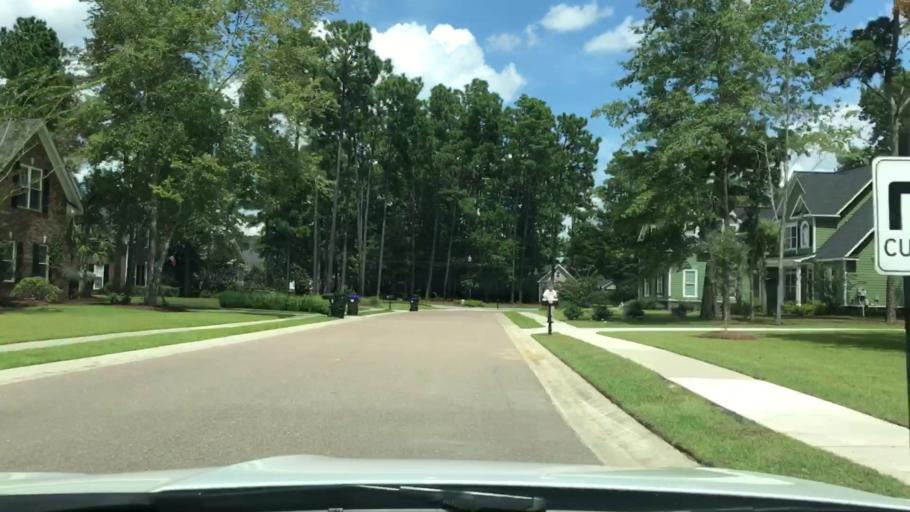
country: US
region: South Carolina
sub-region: Dorchester County
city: Summerville
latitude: 33.0365
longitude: -80.2190
